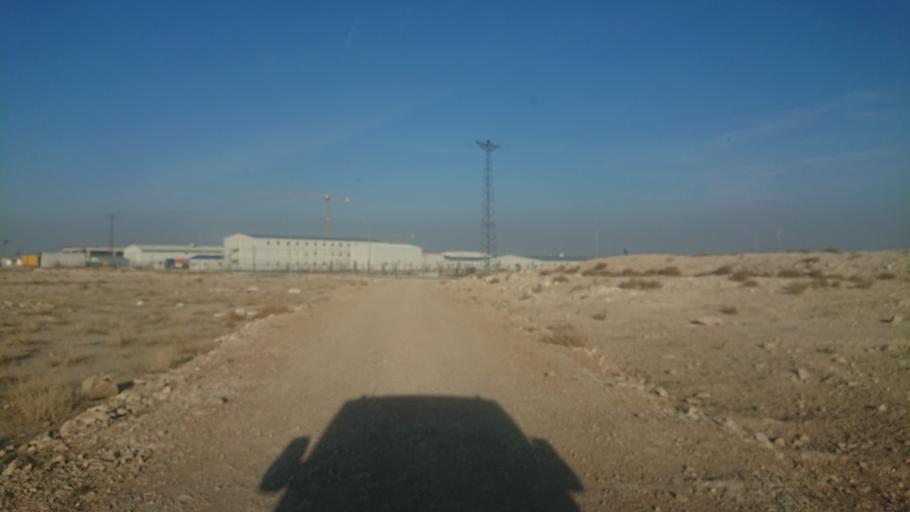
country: TR
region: Aksaray
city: Sultanhani
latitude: 38.1463
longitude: 33.5865
